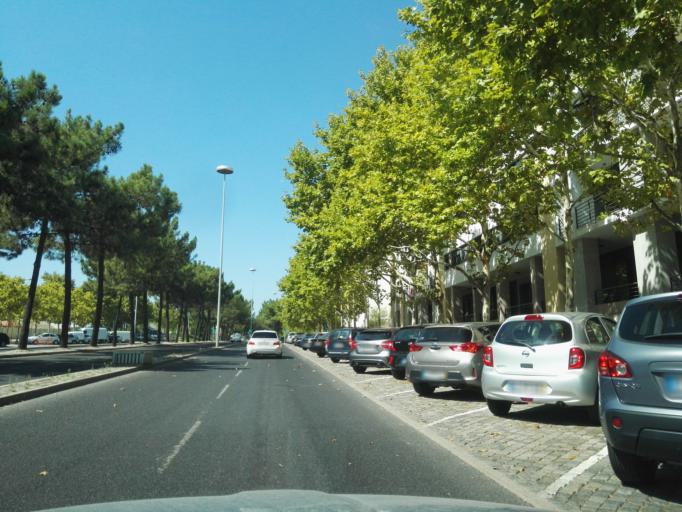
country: PT
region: Lisbon
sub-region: Loures
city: Moscavide
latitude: 38.7793
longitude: -9.0979
